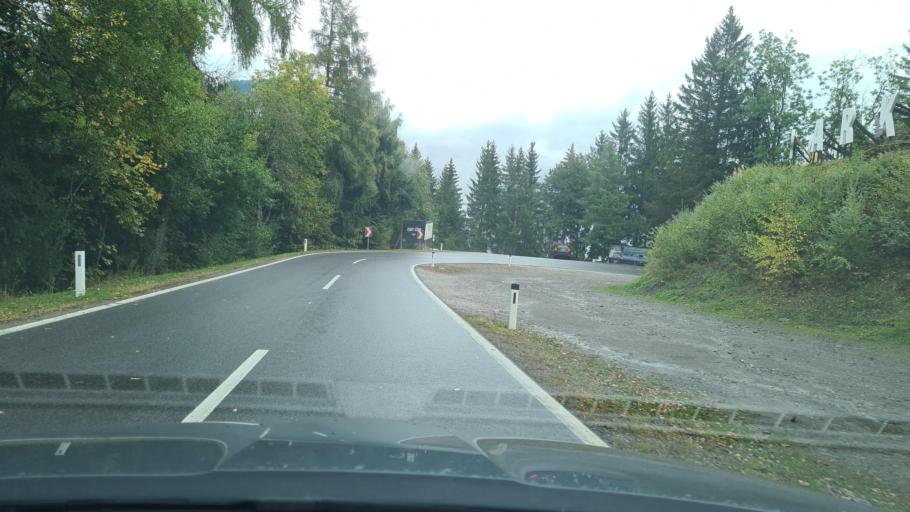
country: AT
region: Styria
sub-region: Politischer Bezirk Weiz
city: Gasen
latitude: 47.3724
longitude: 15.4820
